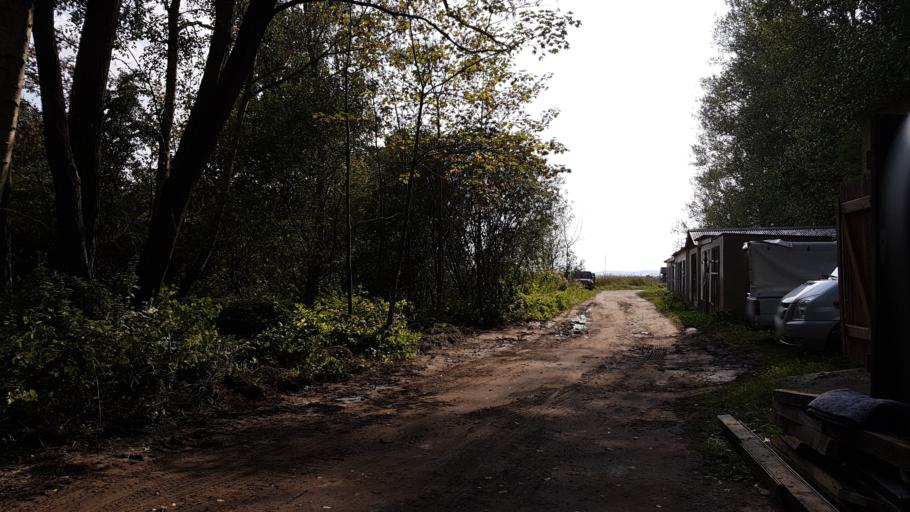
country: DE
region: Mecklenburg-Vorpommern
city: Glowe
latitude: 54.5546
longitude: 13.4840
